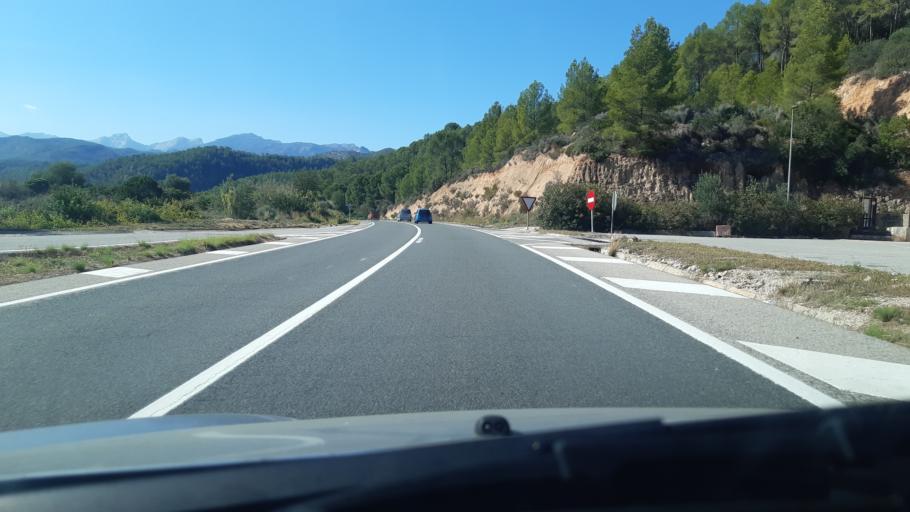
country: ES
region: Catalonia
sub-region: Provincia de Tarragona
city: Benifallet
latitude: 40.9590
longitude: 0.4987
